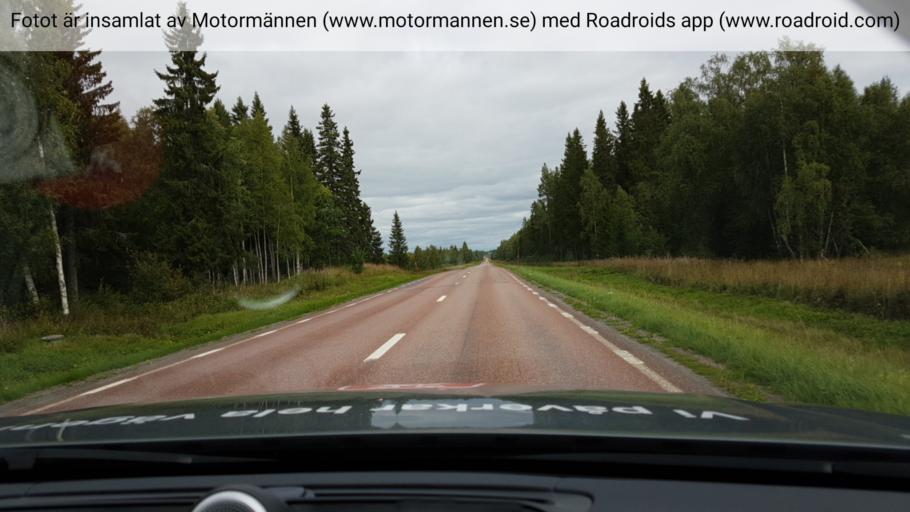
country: SE
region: Jaemtland
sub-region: Stroemsunds Kommun
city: Stroemsund
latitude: 63.7866
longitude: 15.5112
